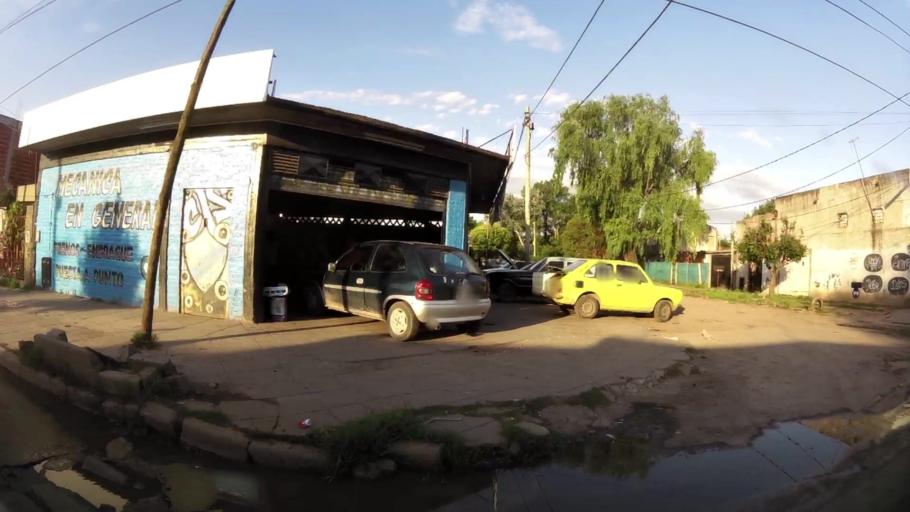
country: AR
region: Buenos Aires
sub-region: Partido de Merlo
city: Merlo
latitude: -34.6874
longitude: -58.7523
